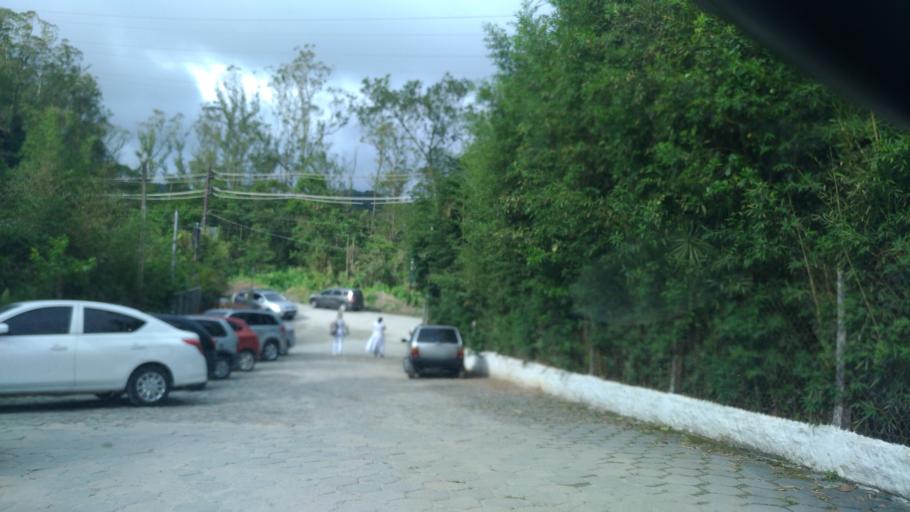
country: BR
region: Sao Paulo
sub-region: Sao Bernardo Do Campo
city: Sao Bernardo do Campo
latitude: -23.7442
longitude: -46.5139
